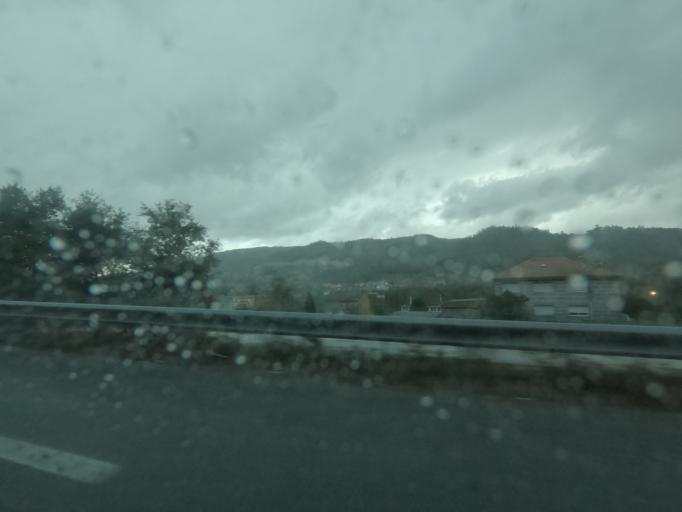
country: ES
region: Galicia
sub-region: Provincia de Pontevedra
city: Pontevedra
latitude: 42.3769
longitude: -8.6361
